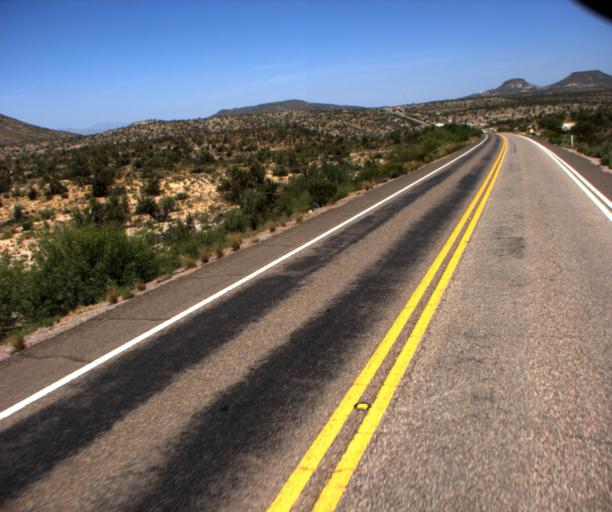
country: US
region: Arizona
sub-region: Gila County
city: Peridot
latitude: 33.2618
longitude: -110.2992
